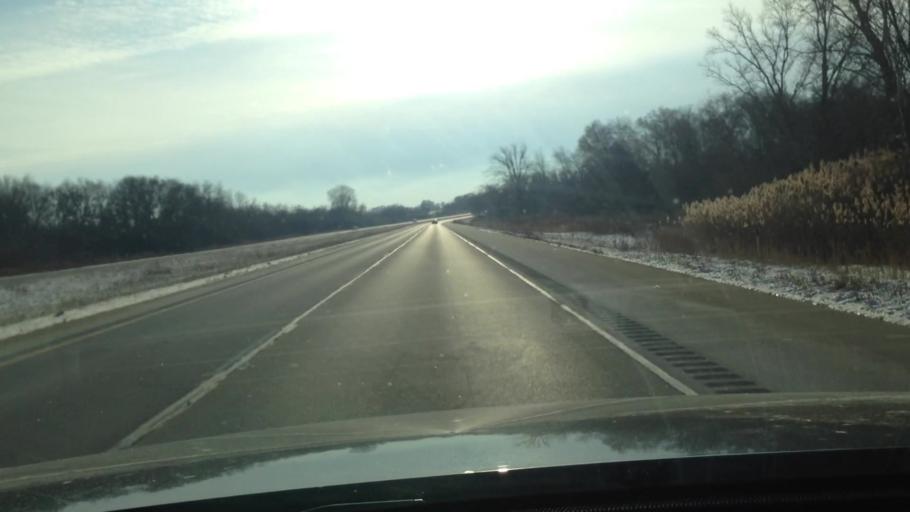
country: US
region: Wisconsin
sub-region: Walworth County
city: Potter Lake
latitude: 42.8121
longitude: -88.3665
